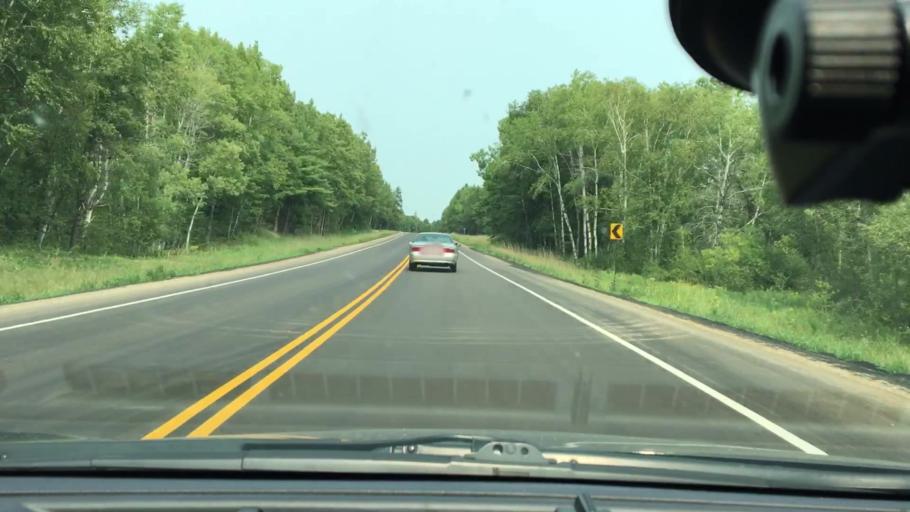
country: US
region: Minnesota
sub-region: Crow Wing County
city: Nisswa
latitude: 46.5238
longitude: -94.2721
